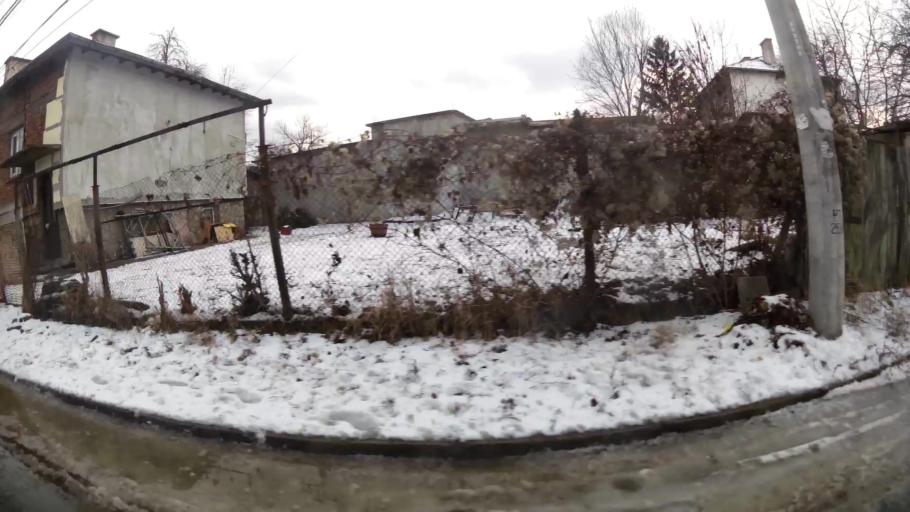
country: BG
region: Sofia-Capital
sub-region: Stolichna Obshtina
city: Sofia
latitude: 42.7219
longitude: 23.3322
